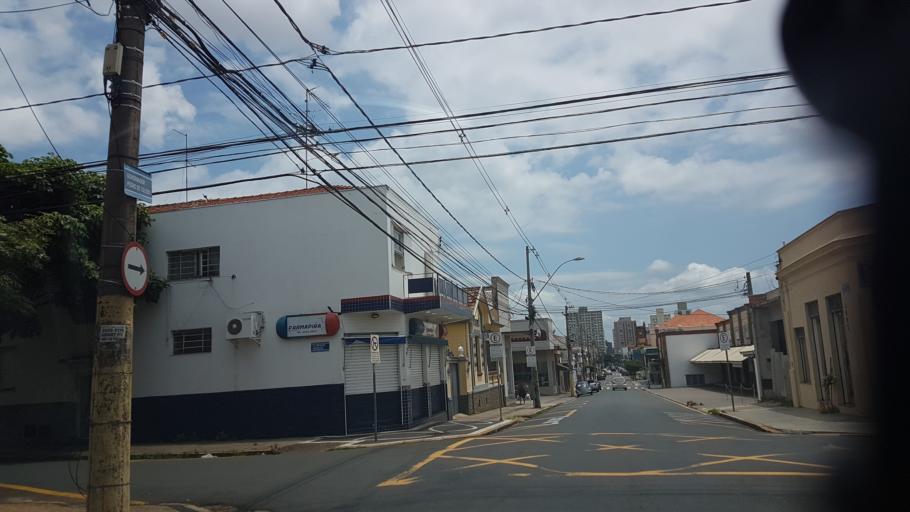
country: BR
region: Sao Paulo
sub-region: Piracicaba
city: Piracicaba
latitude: -22.7320
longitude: -47.6510
